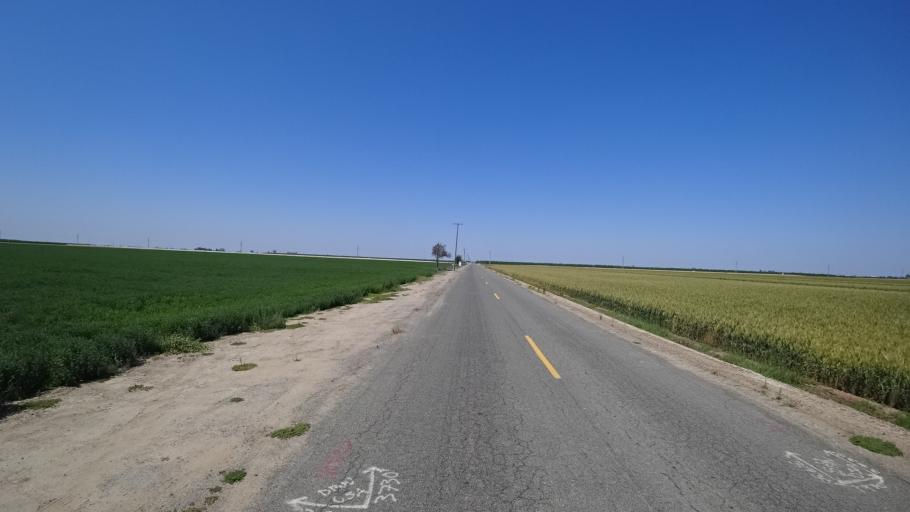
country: US
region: California
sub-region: Kings County
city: Home Garden
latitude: 36.2840
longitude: -119.5854
